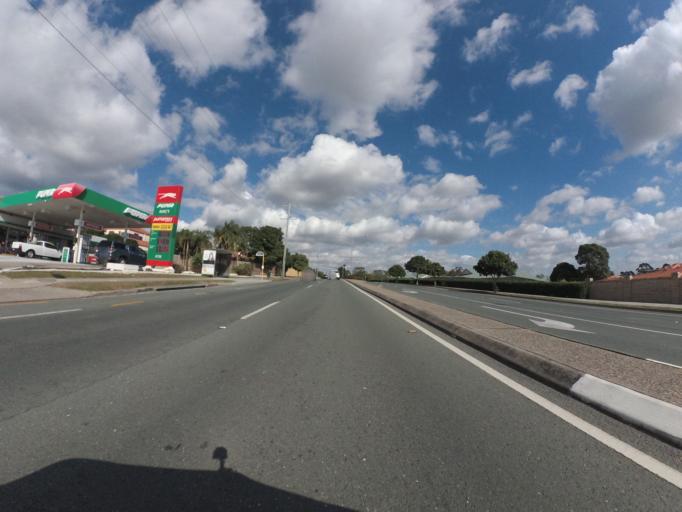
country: AU
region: Queensland
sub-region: Brisbane
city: Wynnum West
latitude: -27.4590
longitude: 153.1515
